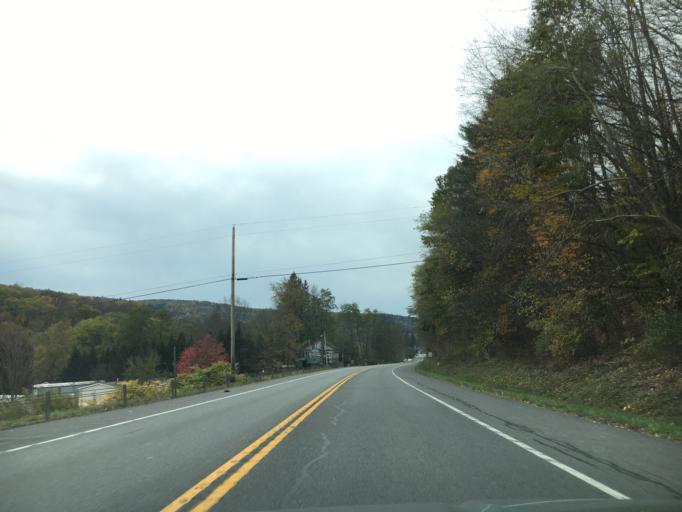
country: US
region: New York
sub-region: Otsego County
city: Oneonta
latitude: 42.5372
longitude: -74.9631
